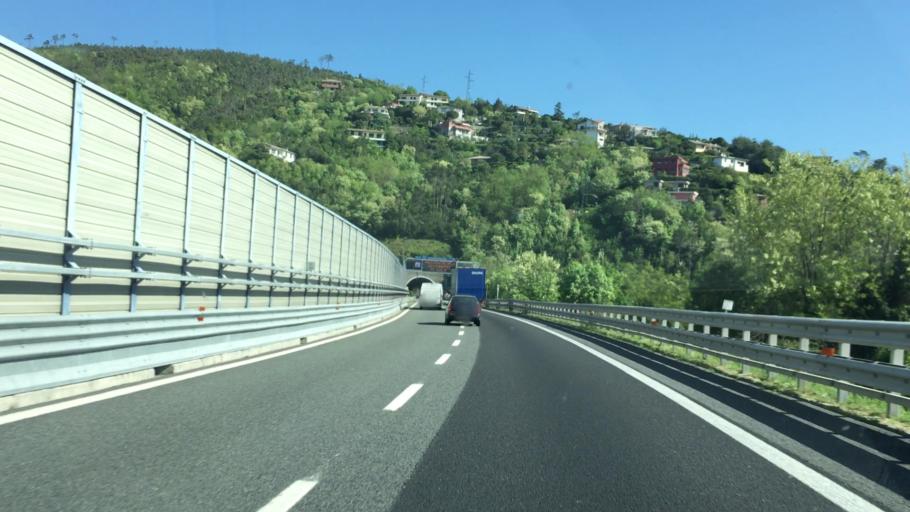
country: IT
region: Liguria
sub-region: Provincia di Genova
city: Sestri Levante
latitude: 44.2933
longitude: 9.3850
